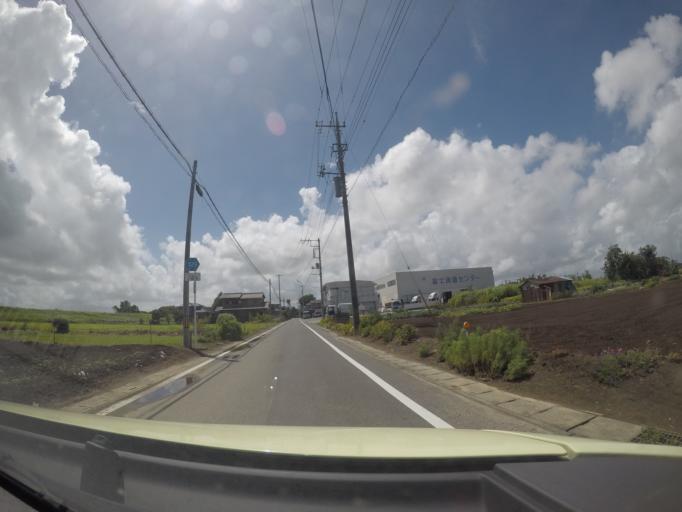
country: JP
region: Ibaraki
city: Mitsukaido
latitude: 36.0646
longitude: 140.0037
